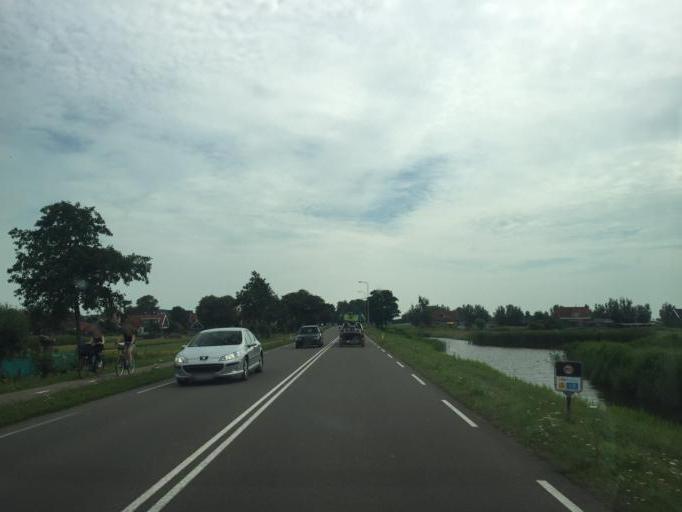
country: NL
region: North Holland
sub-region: Gemeente Heerhugowaard
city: Heerhugowaard
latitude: 52.5989
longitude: 4.8856
